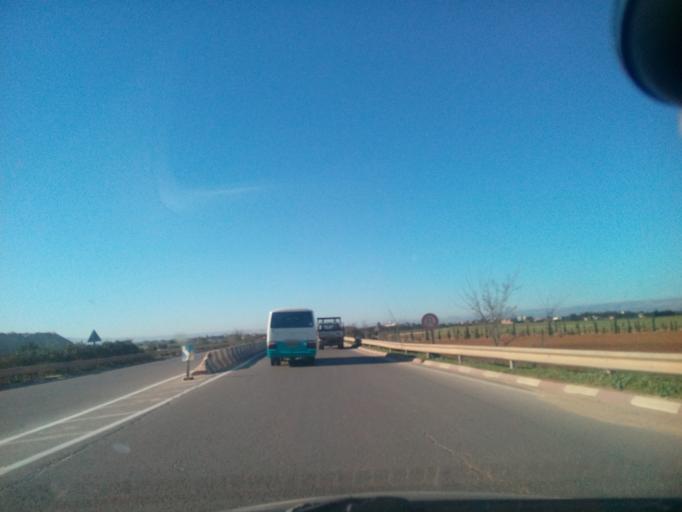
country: DZ
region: Relizane
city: Djidiouia
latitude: 35.8963
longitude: 0.7131
